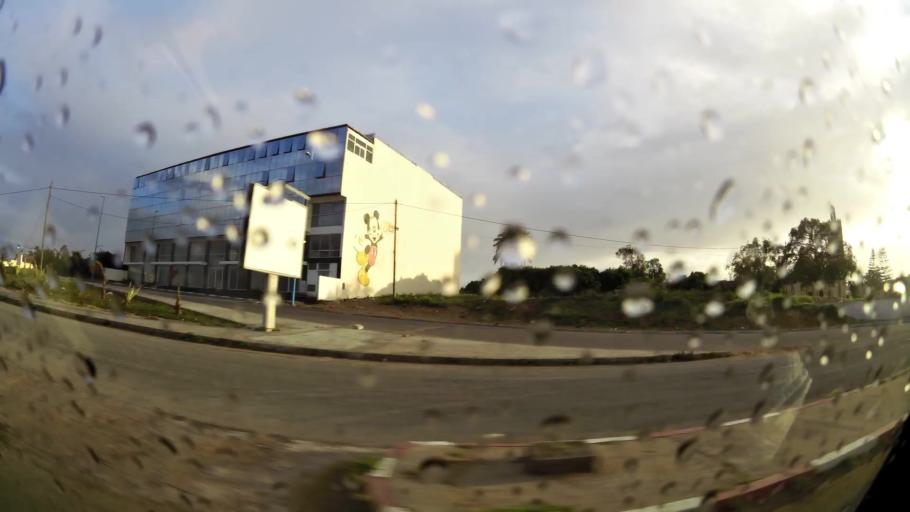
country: MA
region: Doukkala-Abda
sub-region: El-Jadida
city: El Jadida
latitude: 33.2375
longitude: -8.4842
